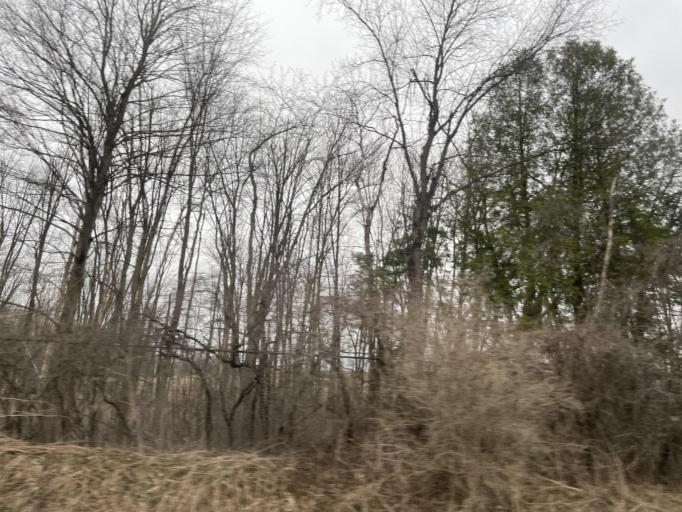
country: CA
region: Ontario
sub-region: Wellington County
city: Guelph
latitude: 43.5790
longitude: -80.2256
